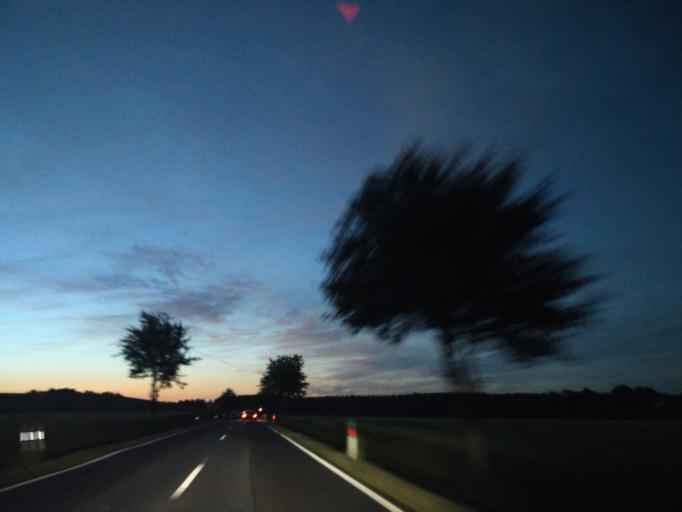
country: HU
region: Vas
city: Vasvar
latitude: 46.9713
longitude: 16.8428
